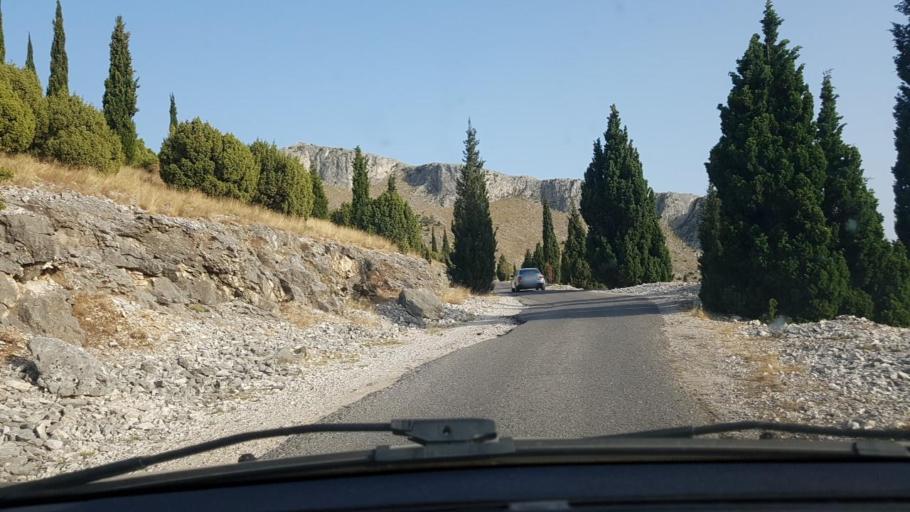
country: BA
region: Federation of Bosnia and Herzegovina
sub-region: Hercegovacko-Bosanski Kanton
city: Mostar
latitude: 43.3490
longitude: 17.8249
